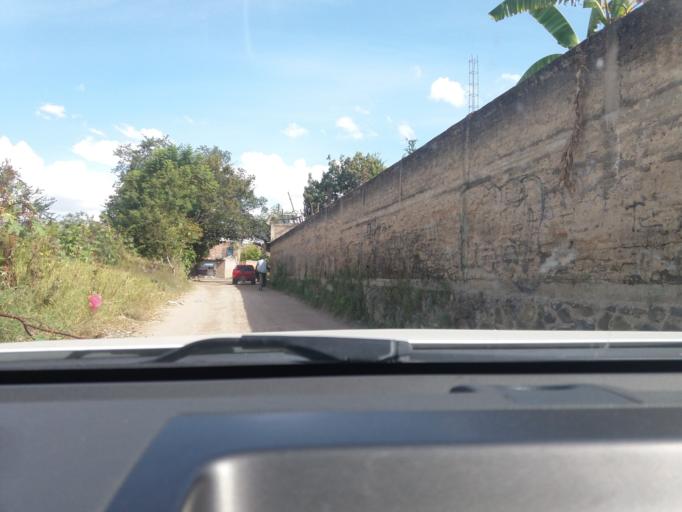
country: MX
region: Jalisco
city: Tala
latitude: 20.6581
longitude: -103.6970
